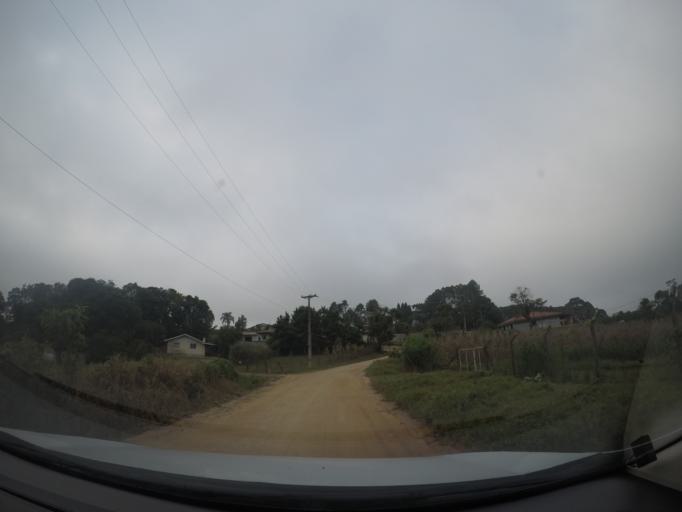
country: BR
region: Parana
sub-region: Colombo
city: Colombo
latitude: -25.3053
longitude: -49.2421
